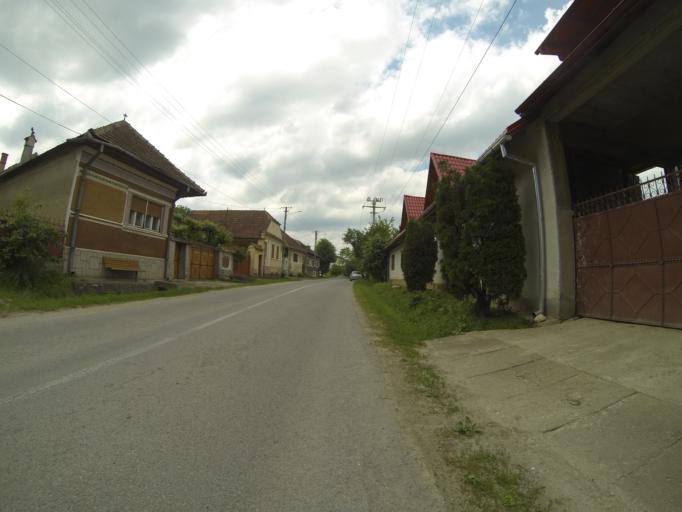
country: RO
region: Brasov
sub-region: Comuna Harseni
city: Harseni
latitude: 45.7403
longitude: 25.0932
